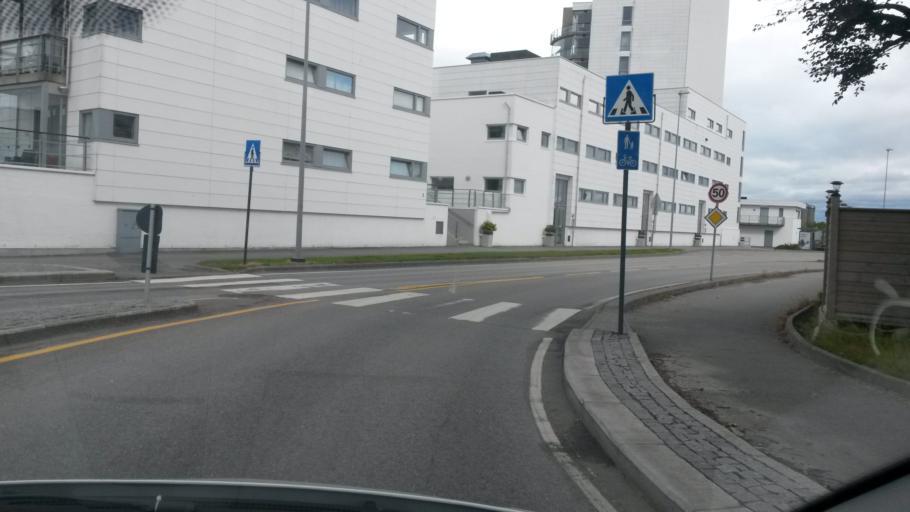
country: NO
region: Rogaland
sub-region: Sandnes
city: Sandnes
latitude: 58.8550
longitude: 5.7498
